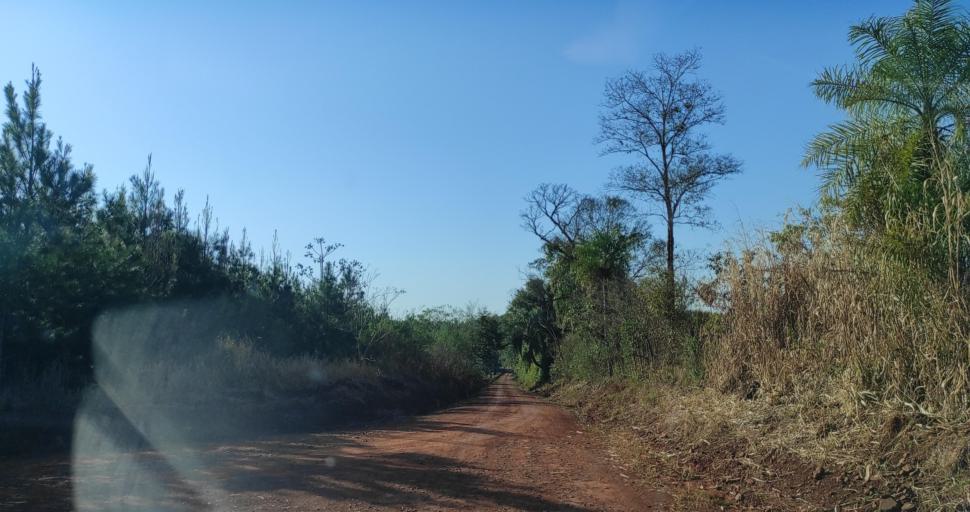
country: AR
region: Misiones
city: Capiovi
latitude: -26.8807
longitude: -55.1077
